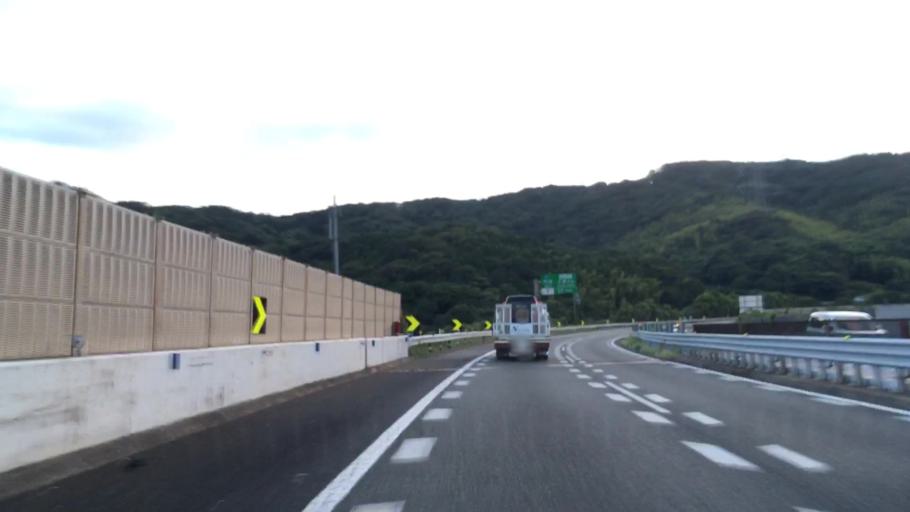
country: JP
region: Yamaguchi
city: Shimonoseki
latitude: 33.9291
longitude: 130.9938
